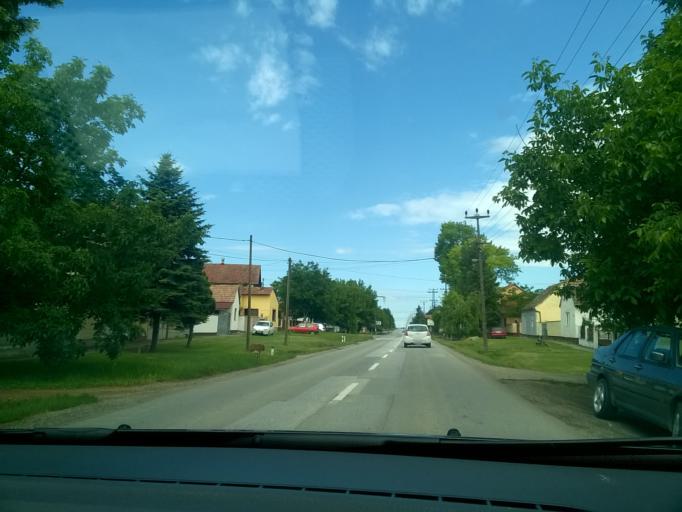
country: RS
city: Putinci
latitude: 45.0012
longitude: 19.9369
